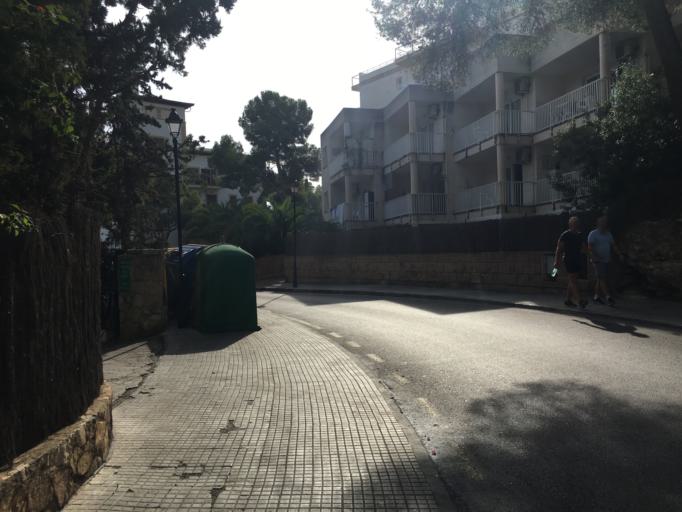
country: ES
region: Balearic Islands
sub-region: Illes Balears
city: Magaluf
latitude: 39.5393
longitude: 2.5913
